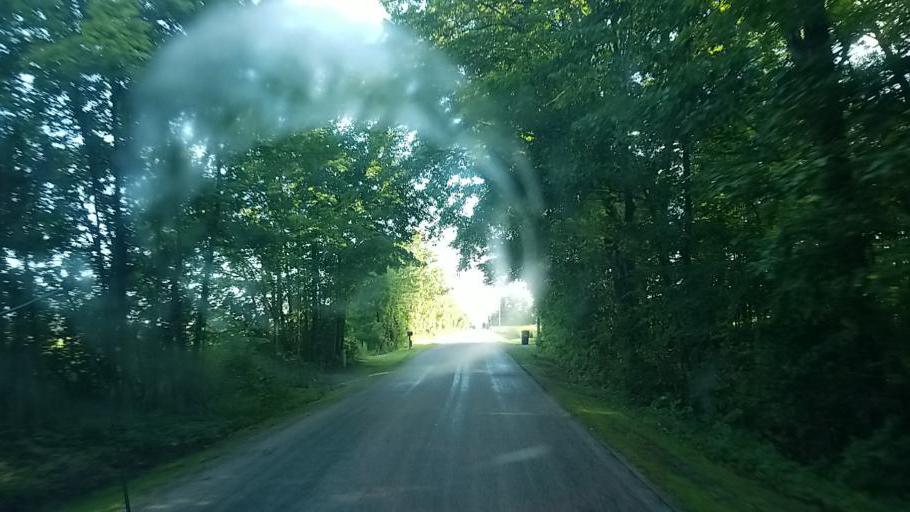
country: US
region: Ohio
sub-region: Crawford County
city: Bucyrus
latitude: 40.7662
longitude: -83.0551
